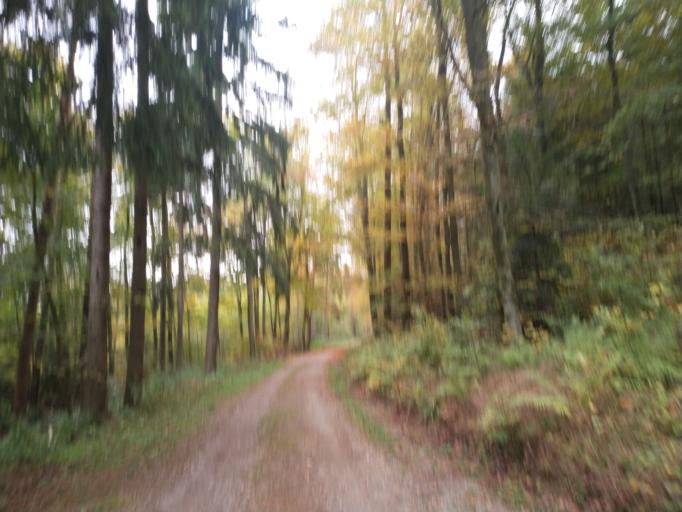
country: DE
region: Baden-Wuerttemberg
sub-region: Karlsruhe Region
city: Birkenfeld
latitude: 48.8607
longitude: 8.6465
